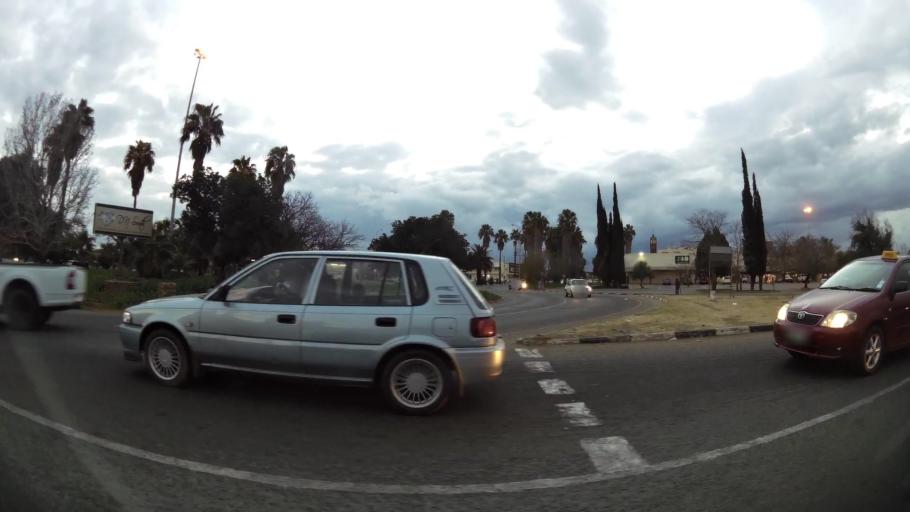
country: ZA
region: Orange Free State
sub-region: Lejweleputswa District Municipality
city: Welkom
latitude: -27.9817
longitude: 26.7425
